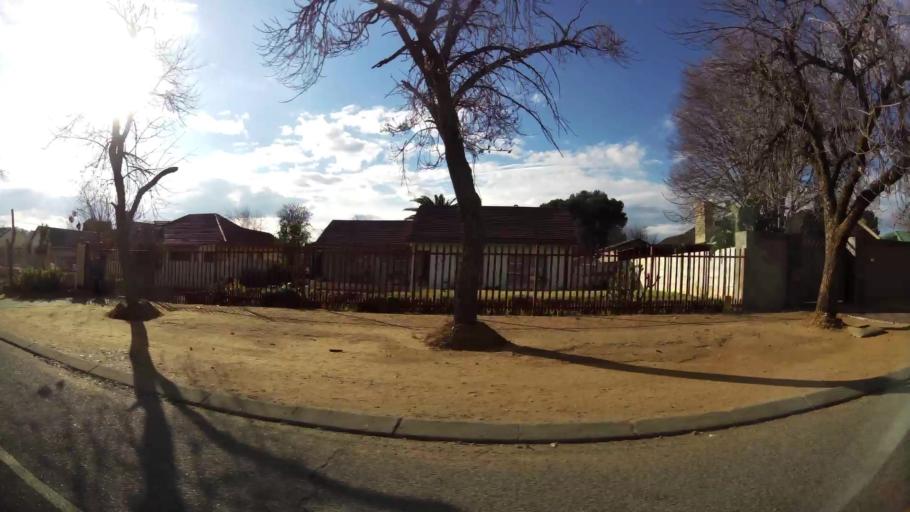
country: ZA
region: Orange Free State
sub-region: Lejweleputswa District Municipality
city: Welkom
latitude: -27.9822
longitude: 26.7191
